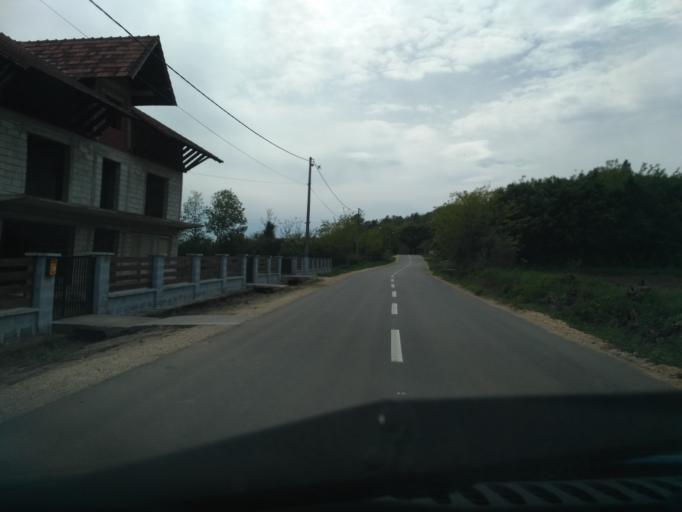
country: RS
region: Central Serbia
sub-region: Podunavski Okrug
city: Smederevska Palanka
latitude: 44.3594
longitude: 21.0147
